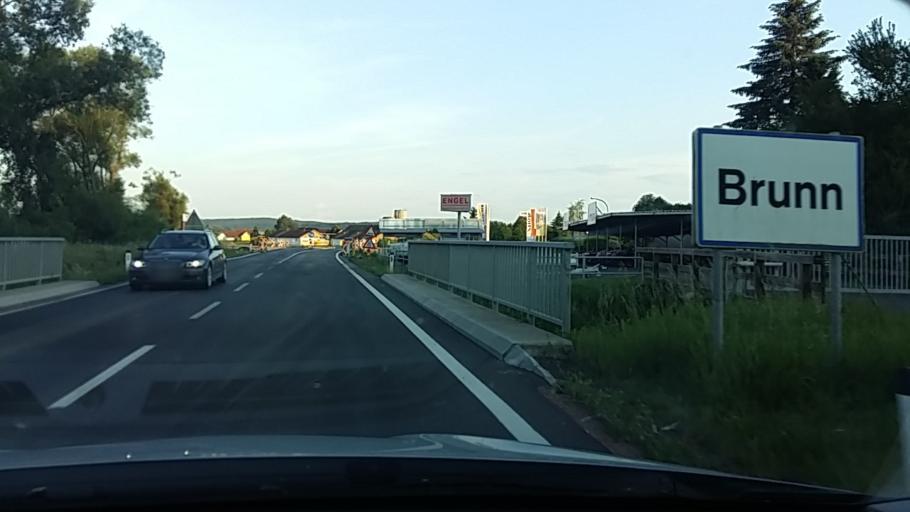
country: AT
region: Styria
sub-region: Politischer Bezirk Suedoststeiermark
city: Fehring
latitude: 46.9586
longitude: 16.0151
